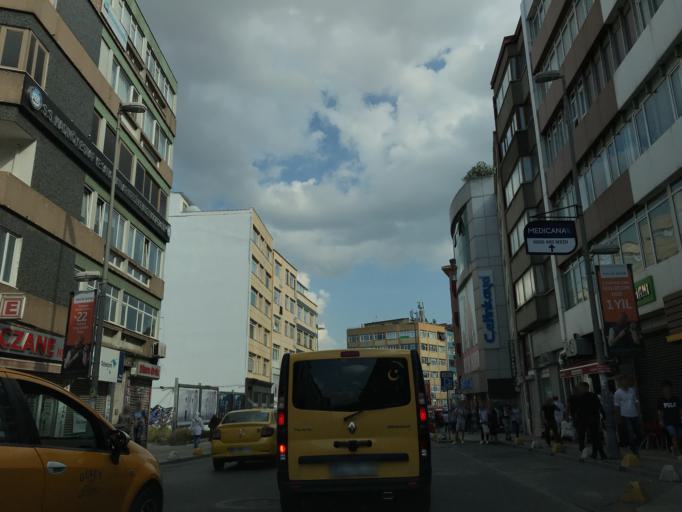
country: TR
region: Istanbul
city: UEskuedar
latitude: 40.9897
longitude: 29.0314
